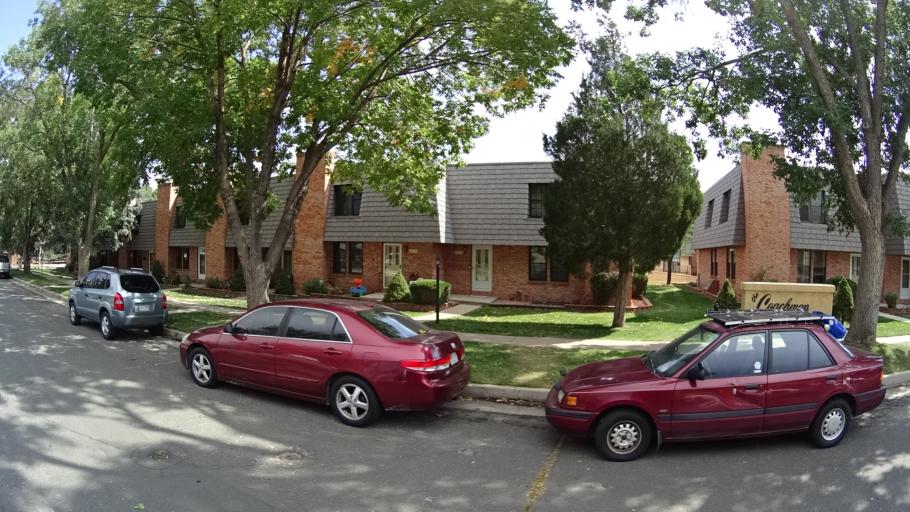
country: US
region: Colorado
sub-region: El Paso County
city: Cimarron Hills
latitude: 38.8623
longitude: -104.7595
